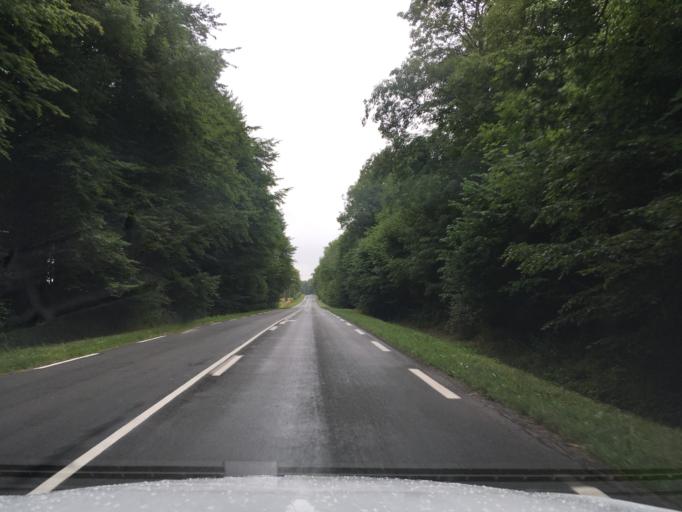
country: FR
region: Picardie
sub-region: Departement de l'Aisne
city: Esqueheries
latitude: 49.9484
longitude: 3.7717
